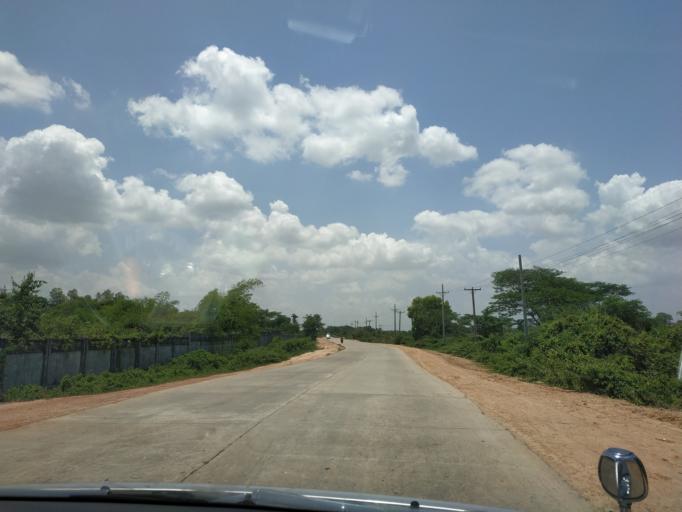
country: MM
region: Bago
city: Bago
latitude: 17.4690
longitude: 96.4579
